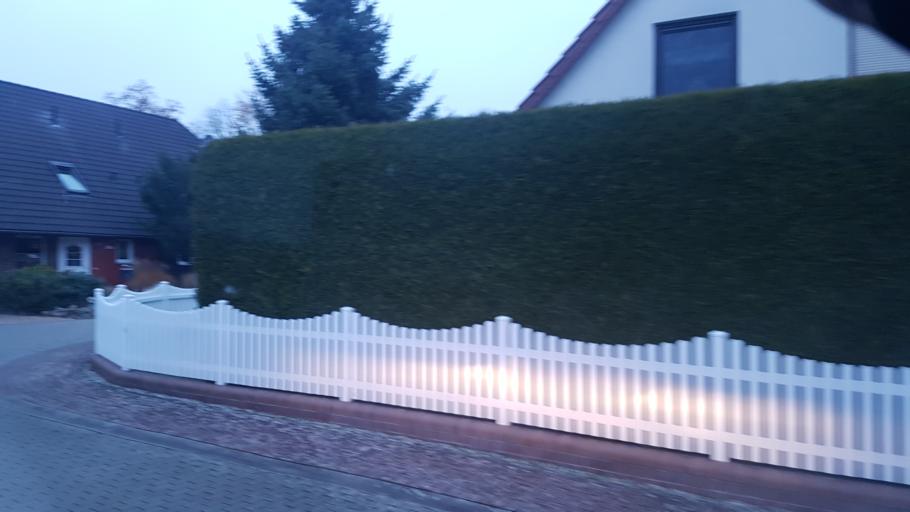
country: DE
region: Brandenburg
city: Vetschau
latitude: 51.8011
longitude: 14.0974
